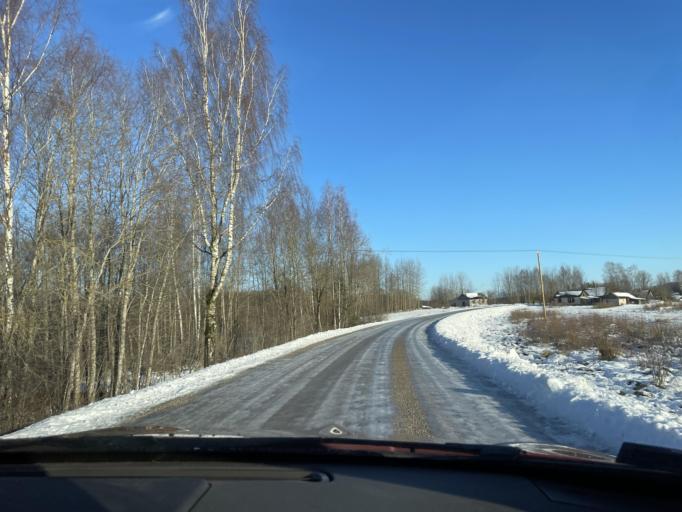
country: LV
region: Ludzas Rajons
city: Ludza
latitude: 56.4680
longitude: 27.5871
